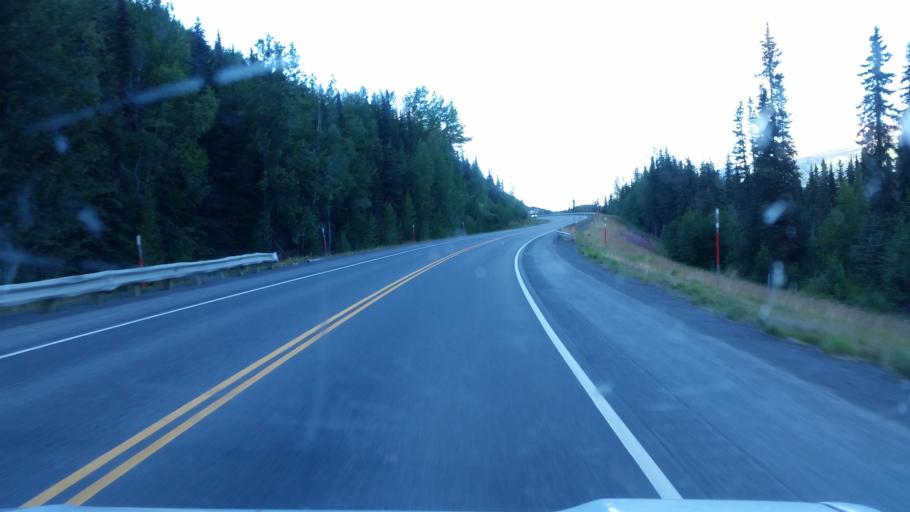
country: US
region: Alaska
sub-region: Kenai Peninsula Borough
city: Bear Creek
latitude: 60.5066
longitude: -149.6875
